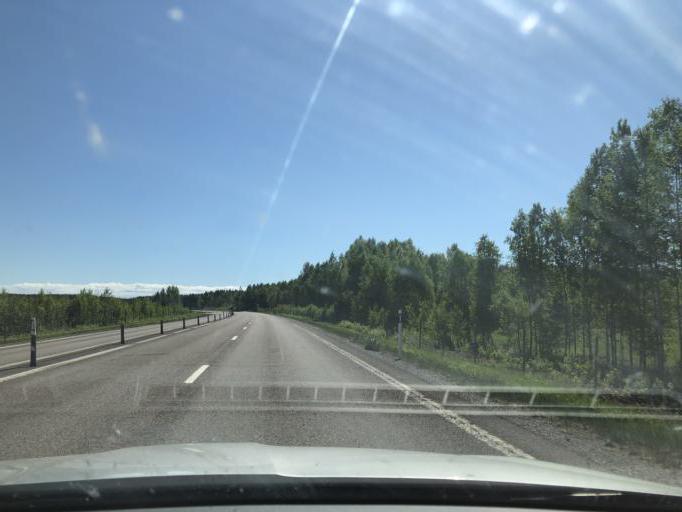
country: SE
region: Norrbotten
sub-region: Kalix Kommun
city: Rolfs
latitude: 65.8859
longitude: 22.9237
